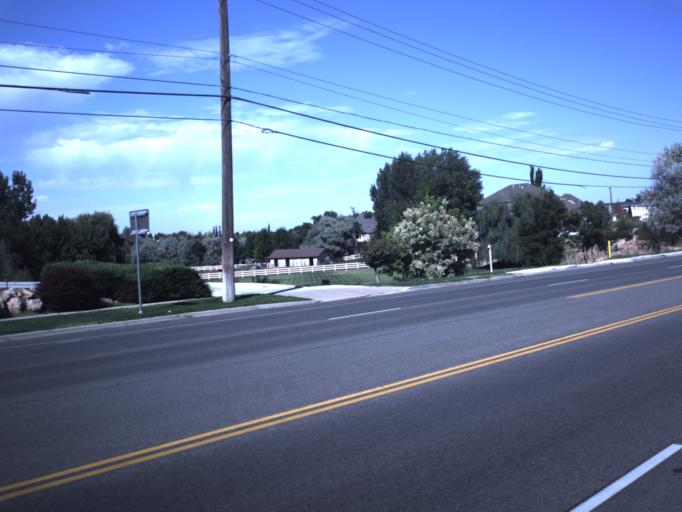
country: US
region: Utah
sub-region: Davis County
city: Fruit Heights
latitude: 41.0166
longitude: -111.9186
